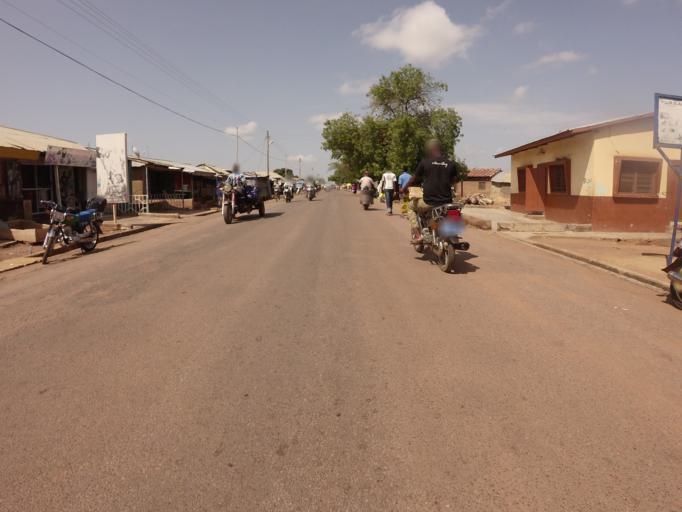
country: GH
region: Upper East
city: Bawku
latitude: 11.0611
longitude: -0.2370
